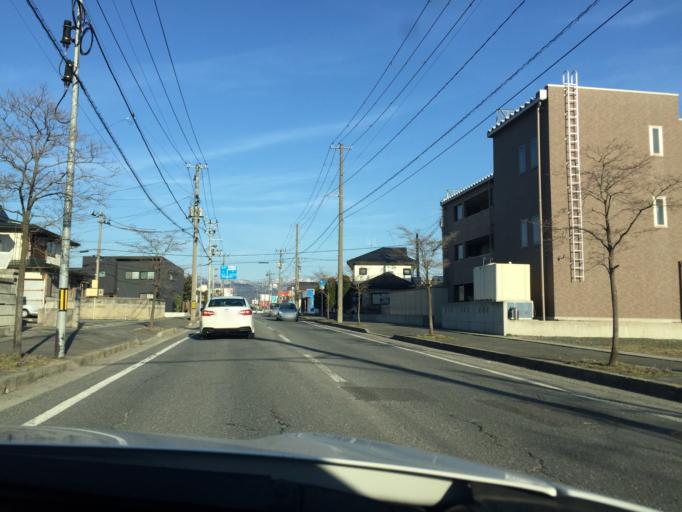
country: JP
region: Yamagata
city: Yonezawa
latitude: 37.9266
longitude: 140.1115
